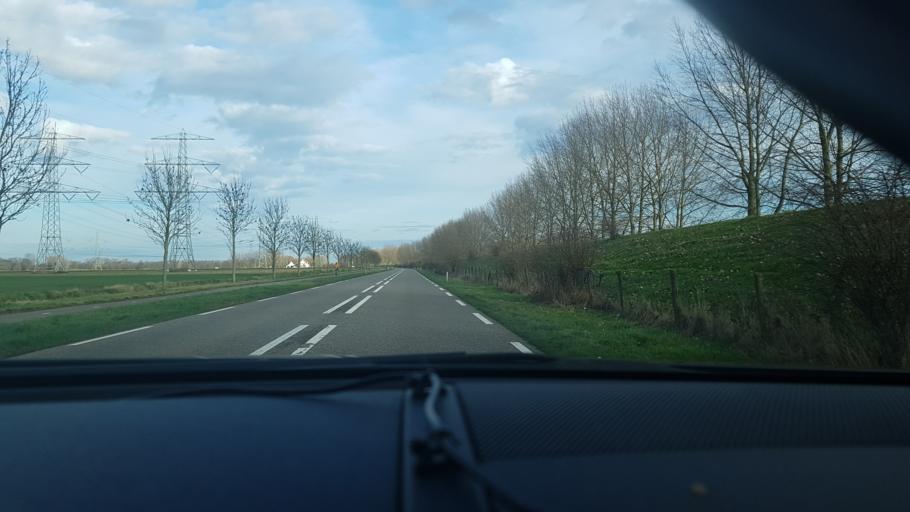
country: NL
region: Limburg
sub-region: Gemeente Leudal
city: Haelen
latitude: 51.2069
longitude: 5.9598
